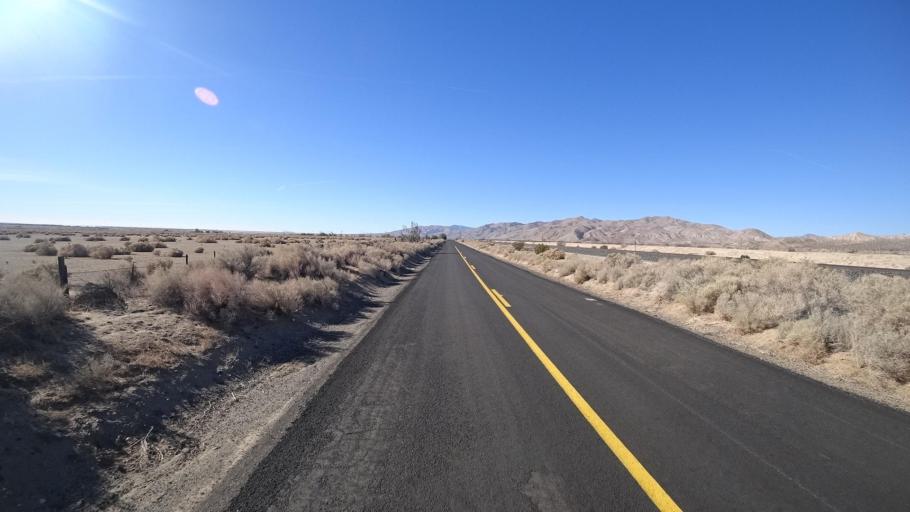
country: US
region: California
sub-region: Kern County
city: California City
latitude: 35.3006
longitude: -117.9816
